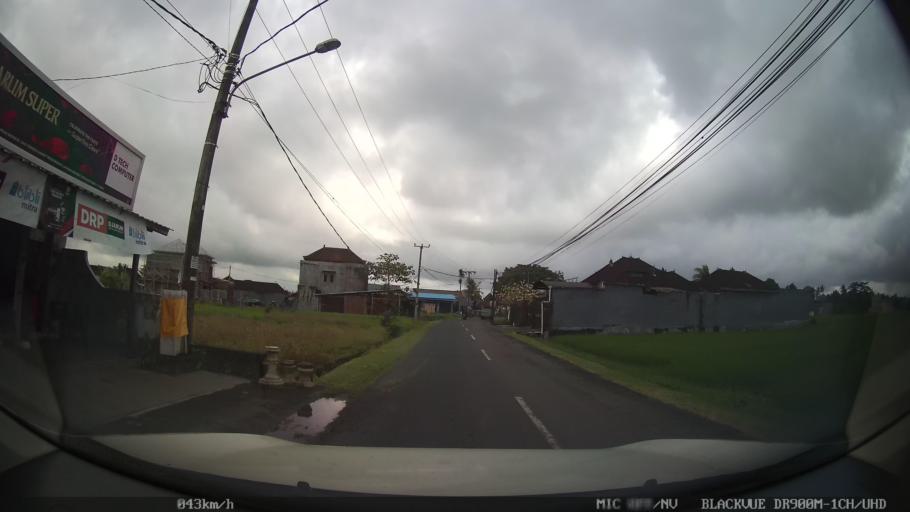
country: ID
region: Bali
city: Banjar Mambalkajanan
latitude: -8.5464
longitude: 115.2130
